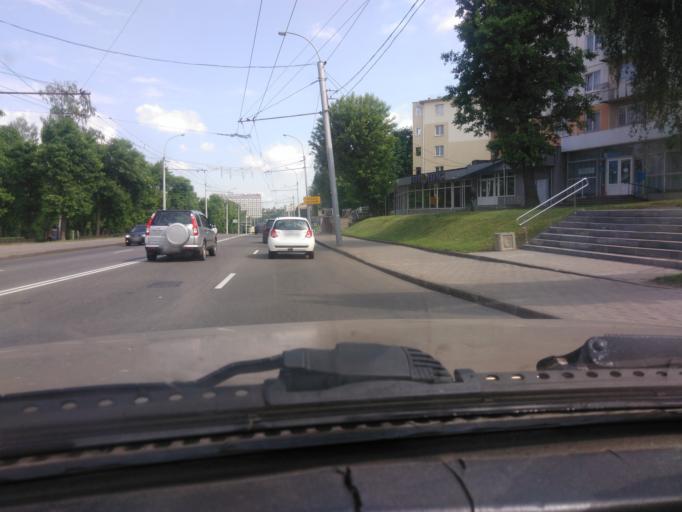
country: BY
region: Mogilev
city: Mahilyow
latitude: 53.9124
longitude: 30.3211
